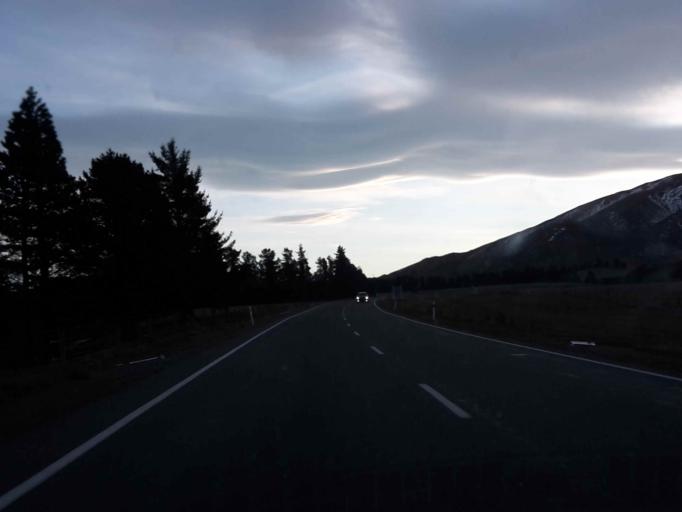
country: NZ
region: Canterbury
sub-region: Timaru District
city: Pleasant Point
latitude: -44.0899
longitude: 170.6487
